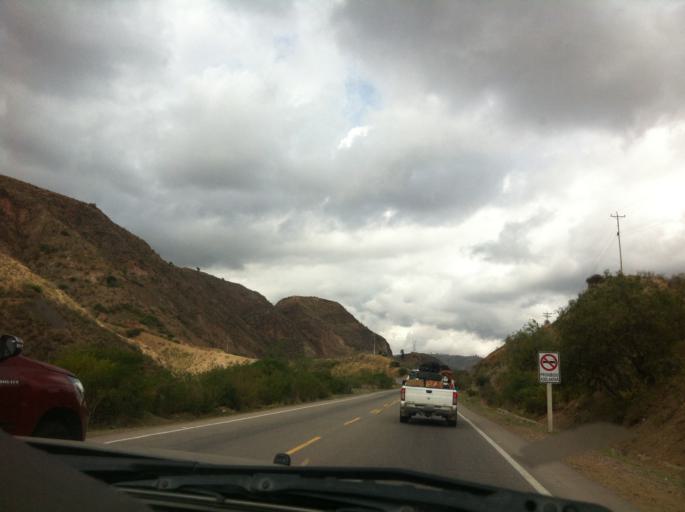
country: BO
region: Cochabamba
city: Irpa Irpa
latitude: -17.6308
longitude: -66.3768
